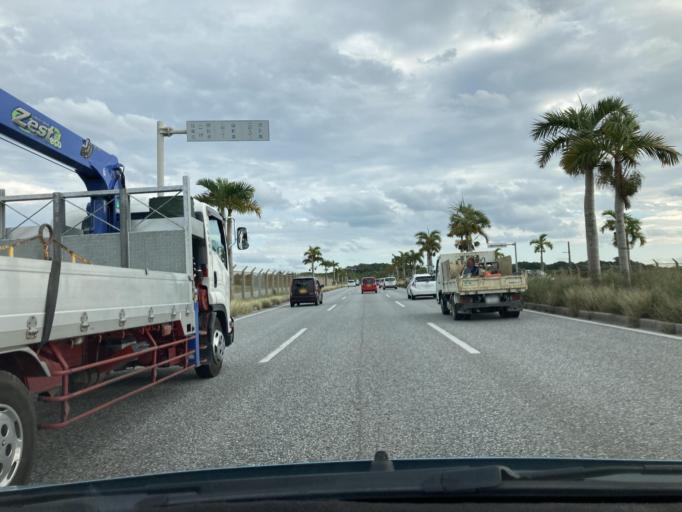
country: JP
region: Okinawa
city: Chatan
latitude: 26.3423
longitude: 127.7494
